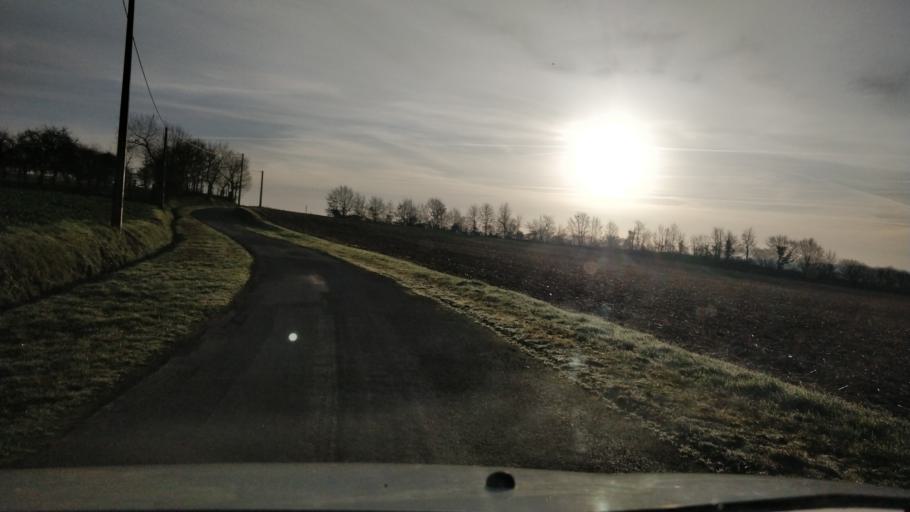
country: FR
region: Brittany
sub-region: Departement d'Ille-et-Vilaine
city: Bais
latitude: 48.0149
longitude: -1.3162
